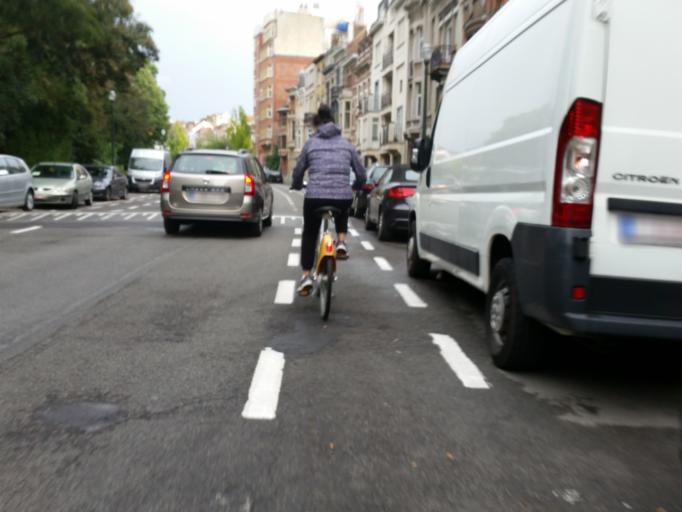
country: BE
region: Brussels Capital
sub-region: Bruxelles-Capitale
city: Brussels
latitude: 50.8608
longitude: 4.3849
